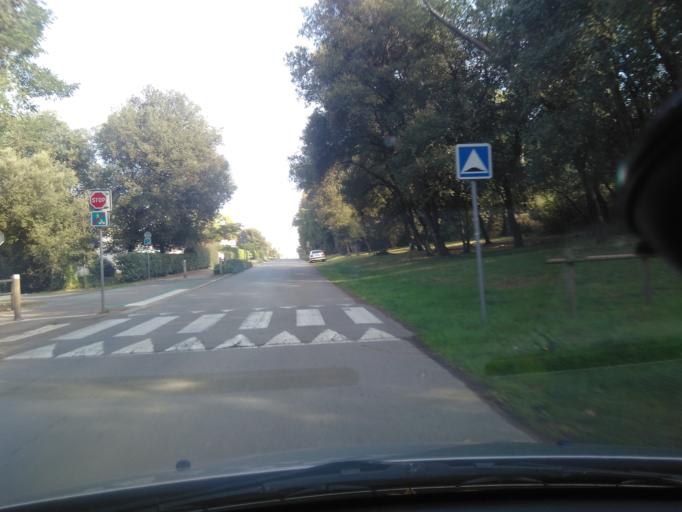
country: FR
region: Pays de la Loire
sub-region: Departement de la Vendee
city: Jard-sur-Mer
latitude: 46.4213
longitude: -1.6047
